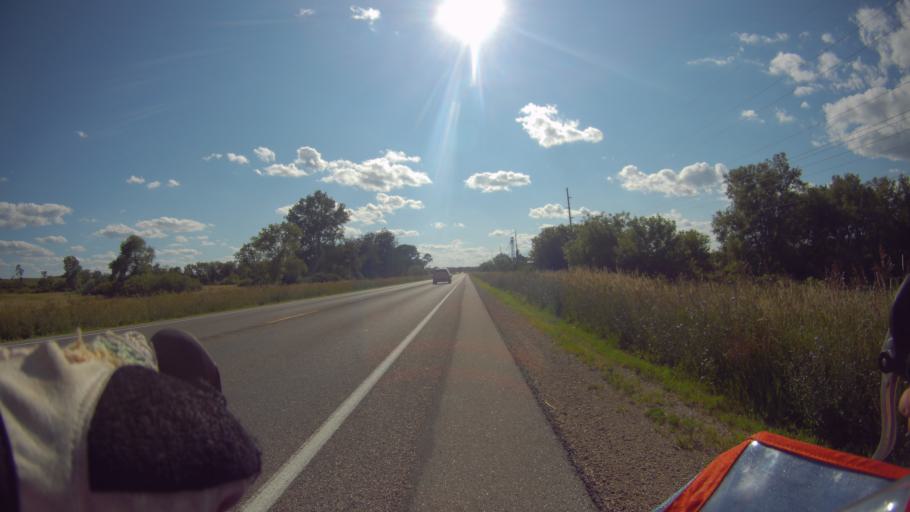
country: US
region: Wisconsin
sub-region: Dane County
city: Oregon
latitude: 42.9180
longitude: -89.3542
